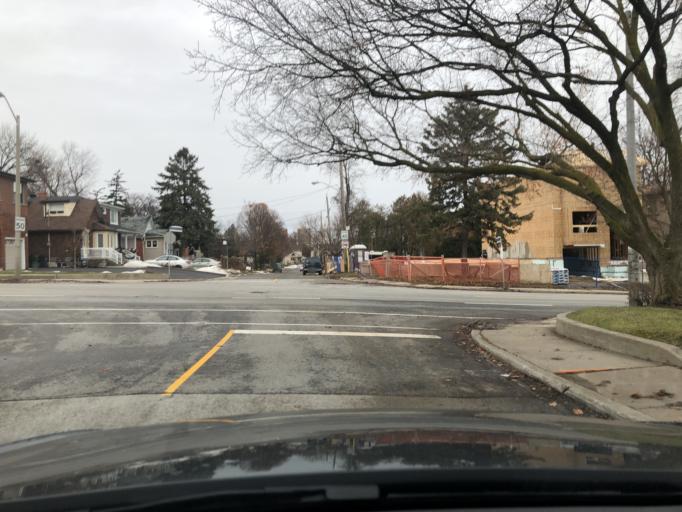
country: CA
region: Ontario
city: Etobicoke
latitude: 43.6967
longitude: -79.5294
